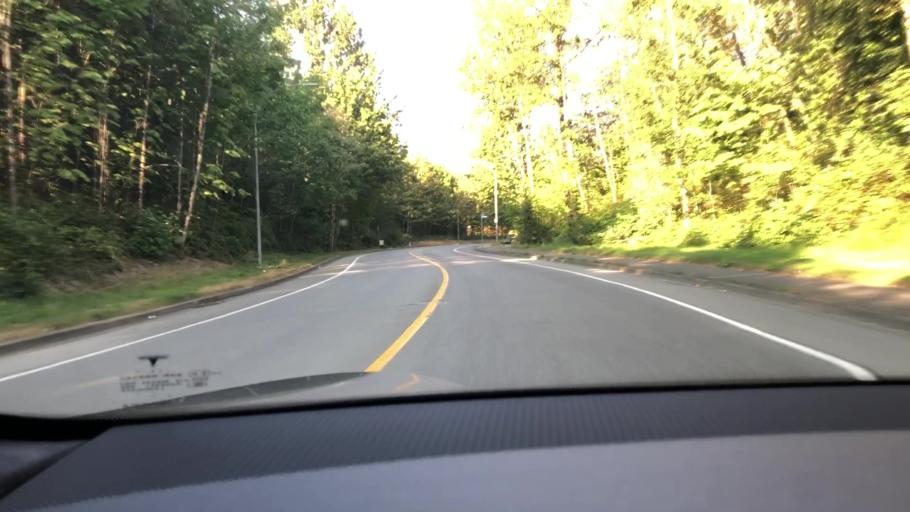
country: CA
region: British Columbia
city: Burnaby
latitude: 49.2289
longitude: -122.9776
